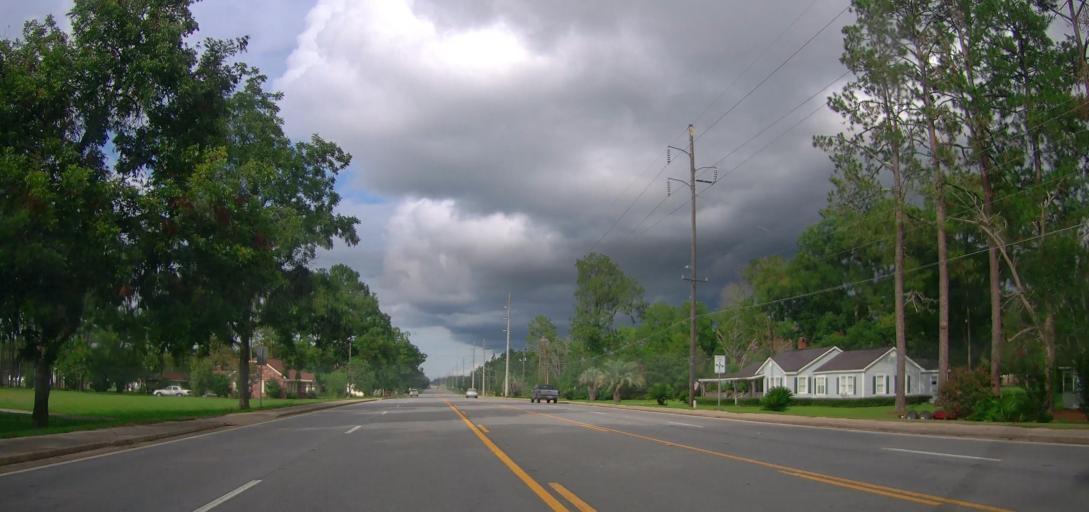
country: US
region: Georgia
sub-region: Pierce County
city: Blackshear
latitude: 31.3901
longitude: -82.1371
